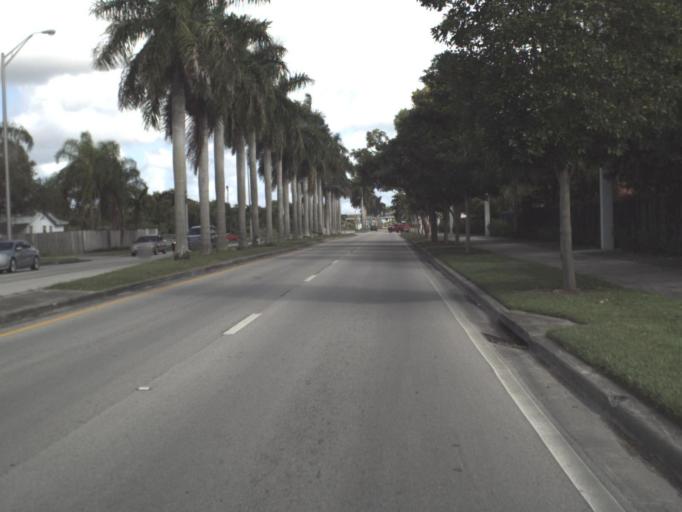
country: US
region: Florida
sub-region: Miami-Dade County
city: Leisure City
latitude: 25.4995
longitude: -80.4224
